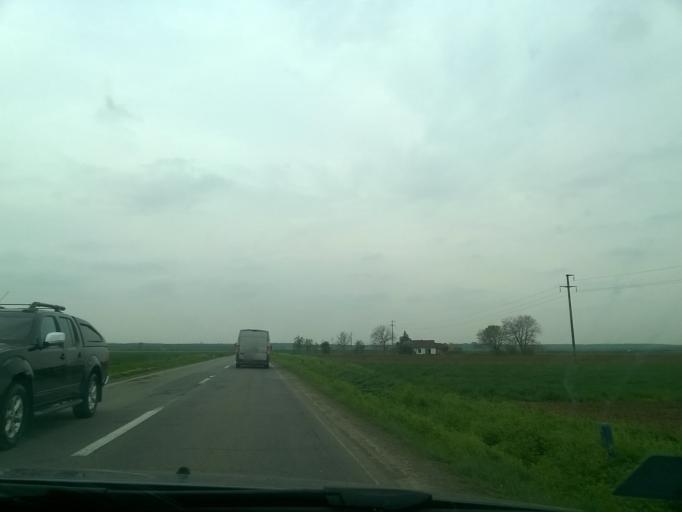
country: RS
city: Platicevo
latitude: 44.8178
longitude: 19.7752
